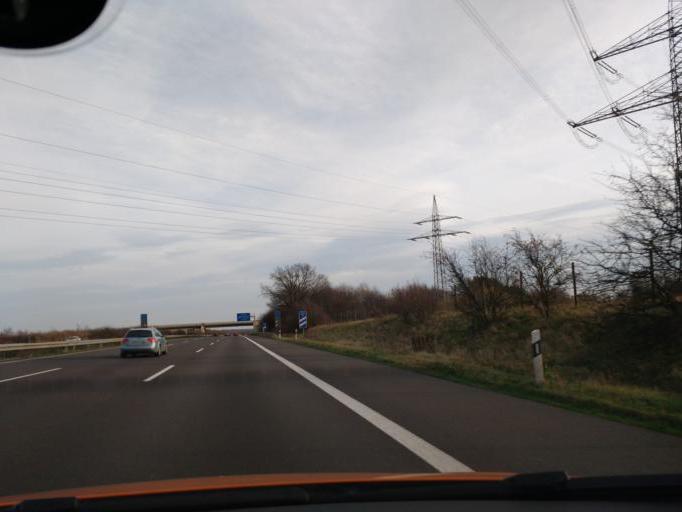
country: DE
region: Lower Saxony
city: Rennau
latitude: 52.2819
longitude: 10.9178
